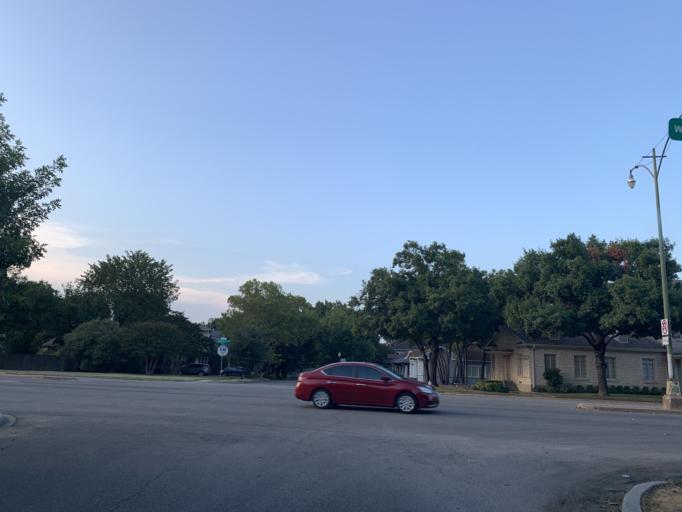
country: US
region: Texas
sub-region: Dallas County
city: Cockrell Hill
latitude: 32.7432
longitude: -96.8417
